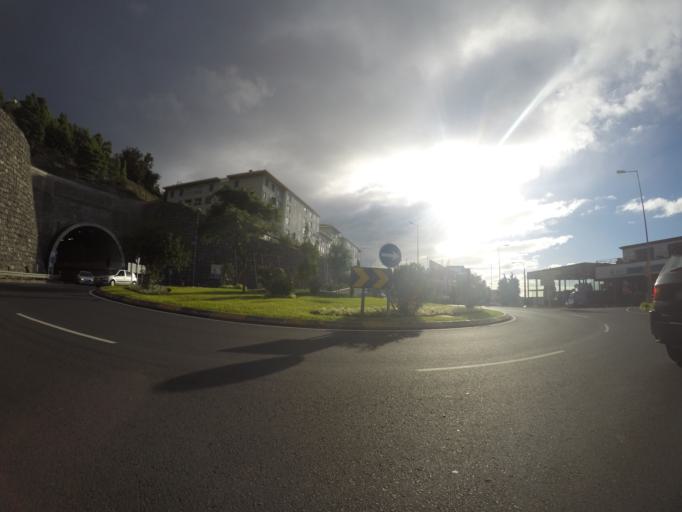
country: PT
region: Madeira
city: Canico
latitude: 32.6484
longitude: -16.8590
